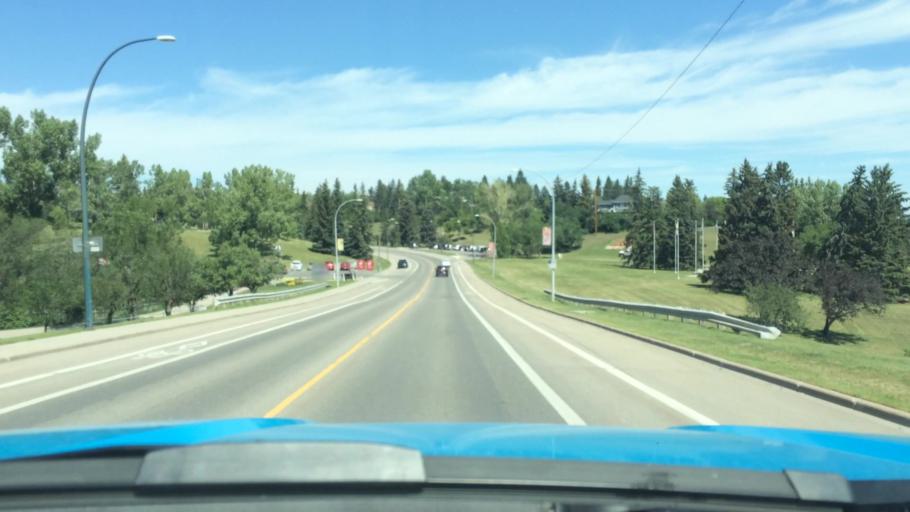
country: CA
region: Alberta
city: Calgary
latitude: 51.0754
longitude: -114.0846
